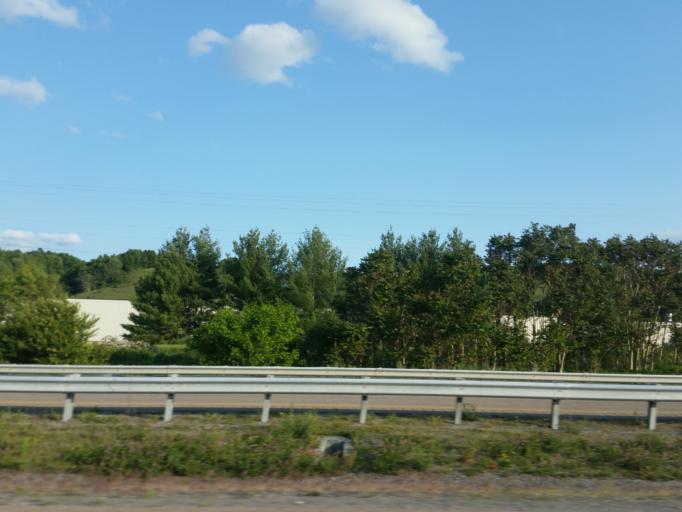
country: US
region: Virginia
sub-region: Russell County
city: Lebanon
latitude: 36.9006
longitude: -82.0529
